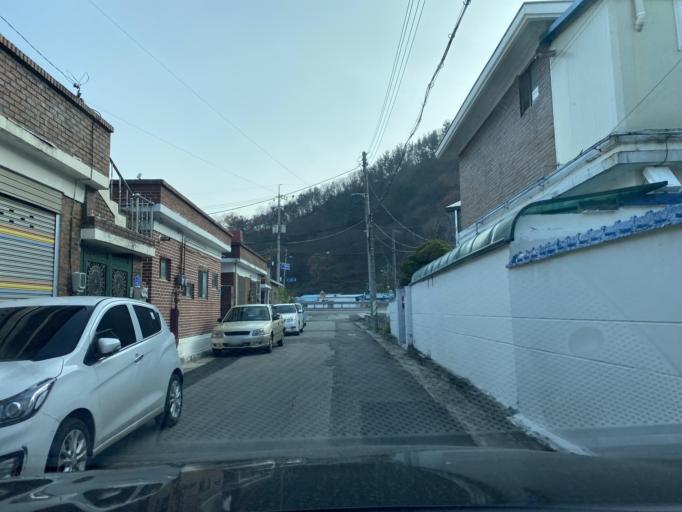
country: KR
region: Chungcheongnam-do
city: Yesan
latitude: 36.6774
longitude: 126.8419
